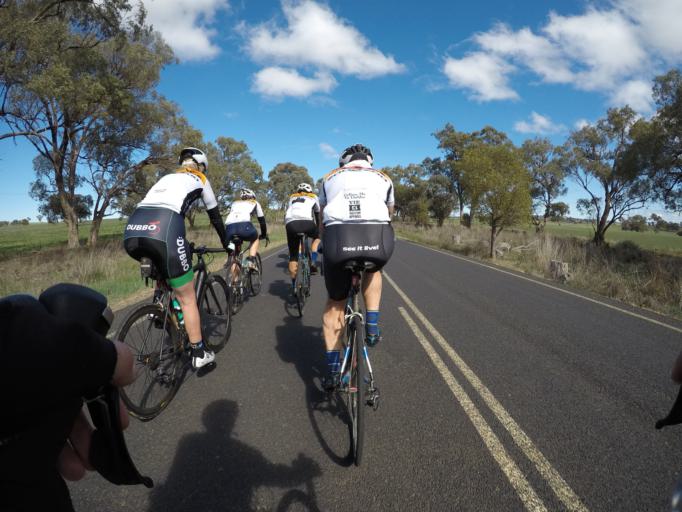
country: AU
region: New South Wales
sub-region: Wellington
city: Wellington
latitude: -32.7508
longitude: 148.6203
